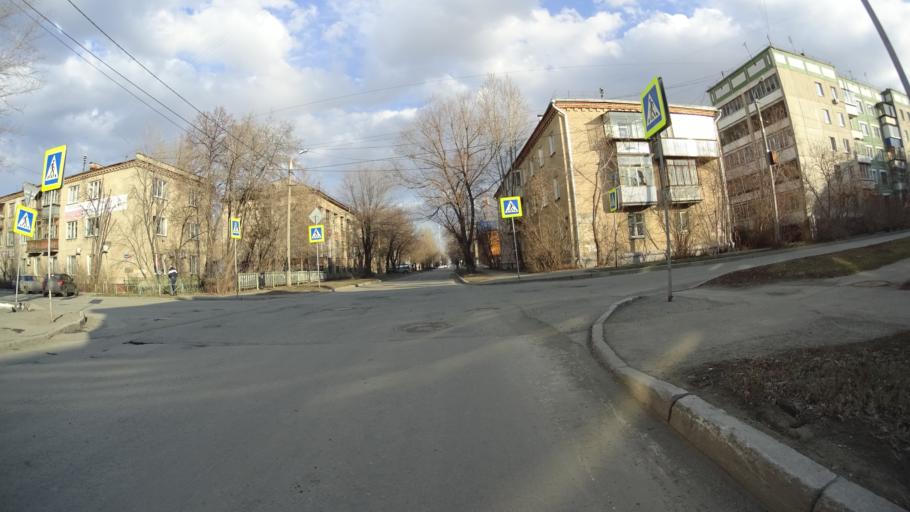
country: RU
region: Chelyabinsk
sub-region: Gorod Chelyabinsk
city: Chelyabinsk
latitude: 55.1435
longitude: 61.3810
